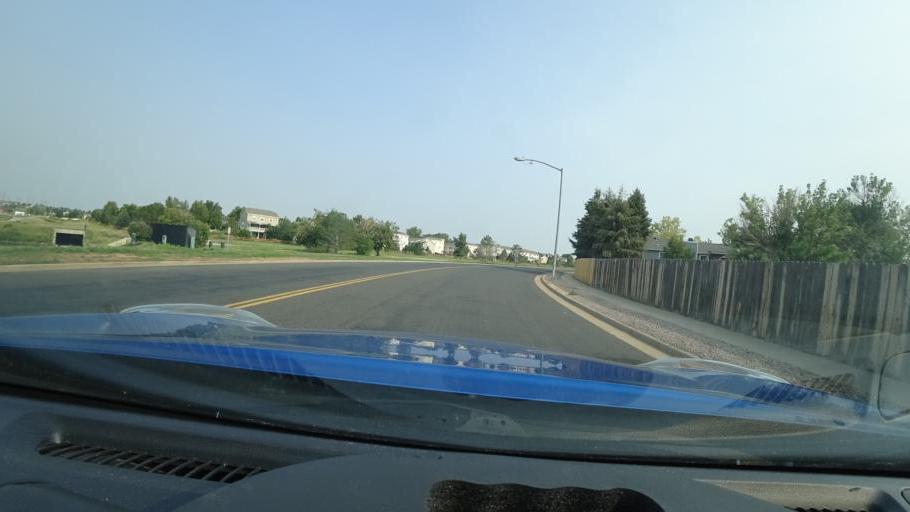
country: US
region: Colorado
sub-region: Adams County
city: Aurora
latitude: 39.6664
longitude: -104.7797
